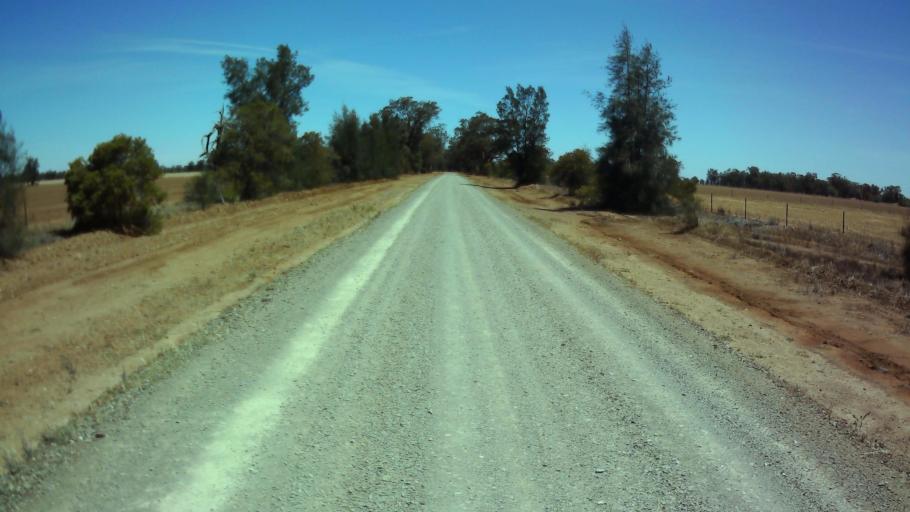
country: AU
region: New South Wales
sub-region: Weddin
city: Grenfell
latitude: -33.9077
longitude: 147.6851
